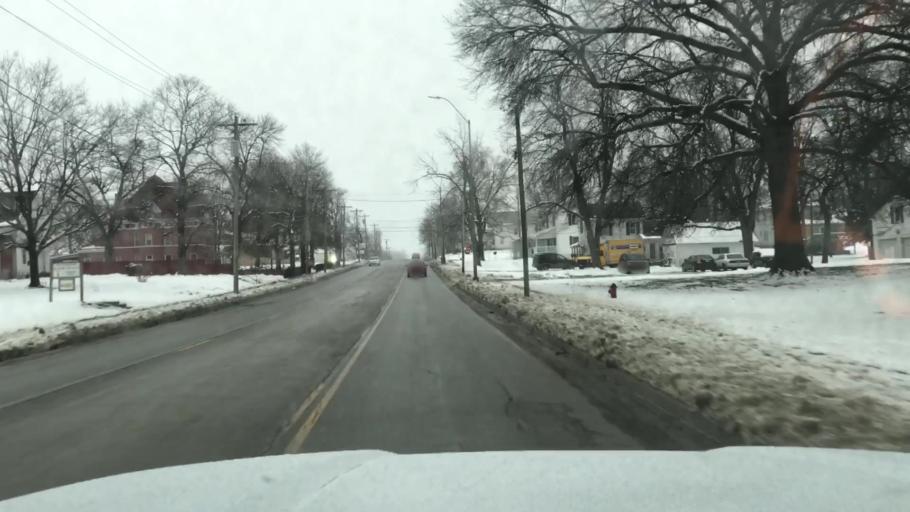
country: US
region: Missouri
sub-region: Clinton County
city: Cameron
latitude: 39.7355
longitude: -94.2361
